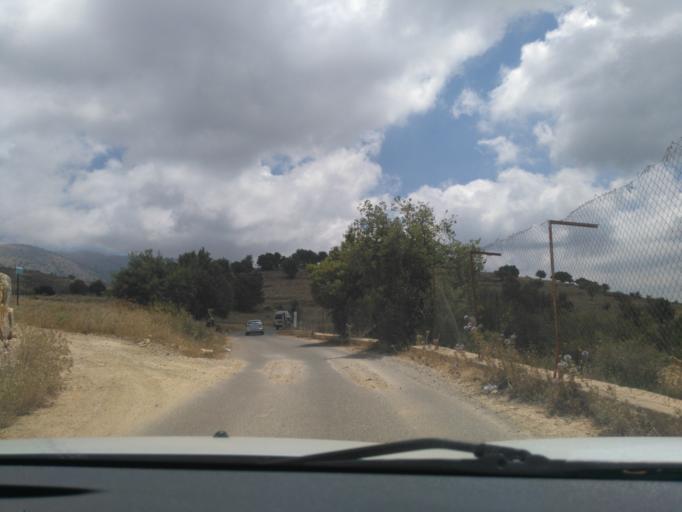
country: LB
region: Mont-Liban
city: Beit ed Dine
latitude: 33.6876
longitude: 35.6676
